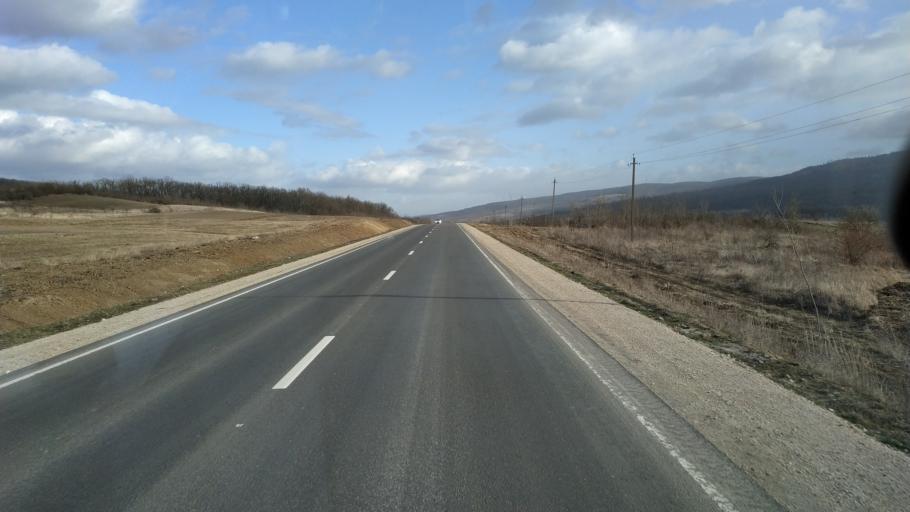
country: MD
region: Calarasi
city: Calarasi
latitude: 47.3119
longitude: 28.1218
